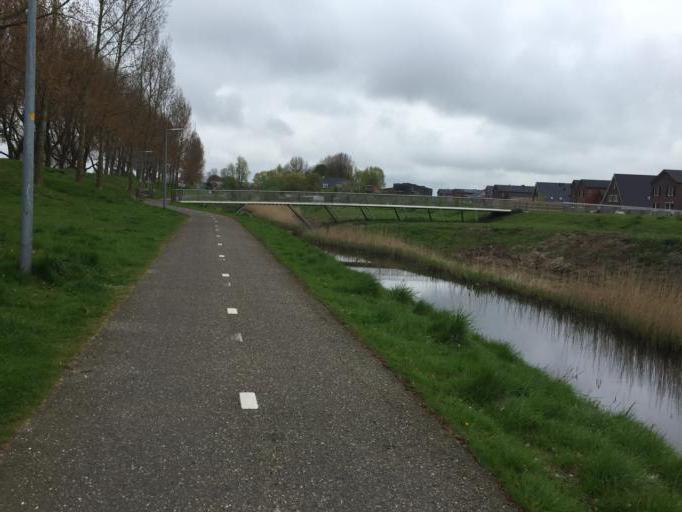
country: NL
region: North Holland
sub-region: Gemeente Haarlemmermeer
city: Hoofddorp
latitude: 52.3429
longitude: 4.6728
